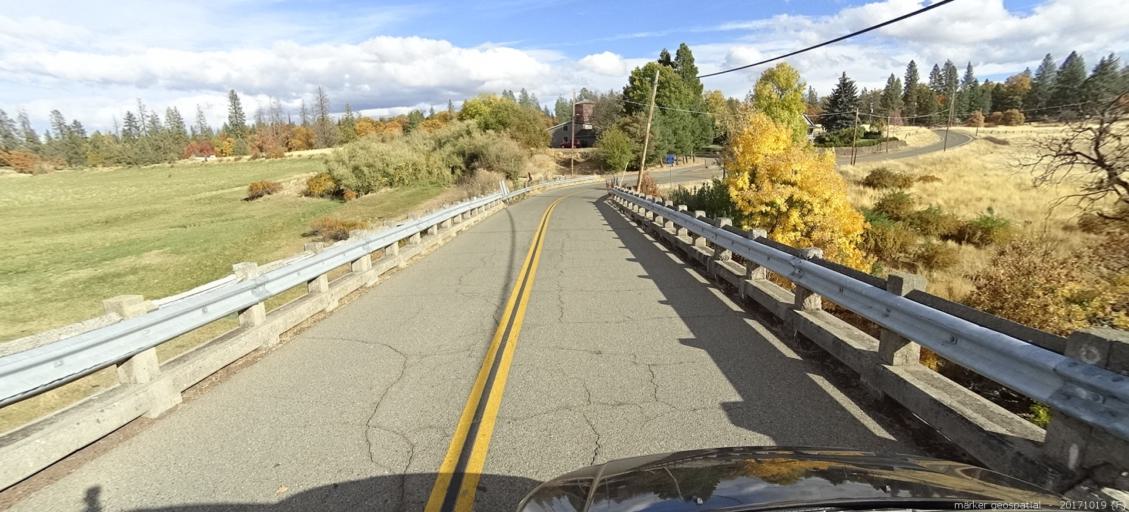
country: US
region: California
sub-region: Shasta County
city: Burney
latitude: 41.0010
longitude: -121.4361
